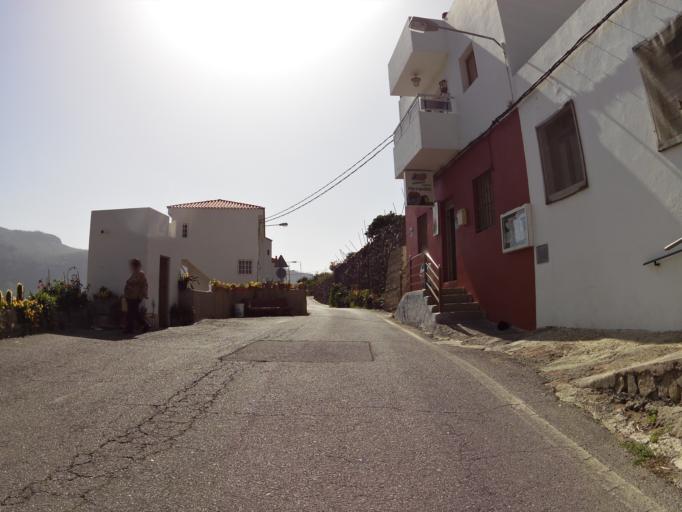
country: ES
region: Canary Islands
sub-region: Provincia de Las Palmas
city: Mogan
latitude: 27.8955
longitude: -15.6777
